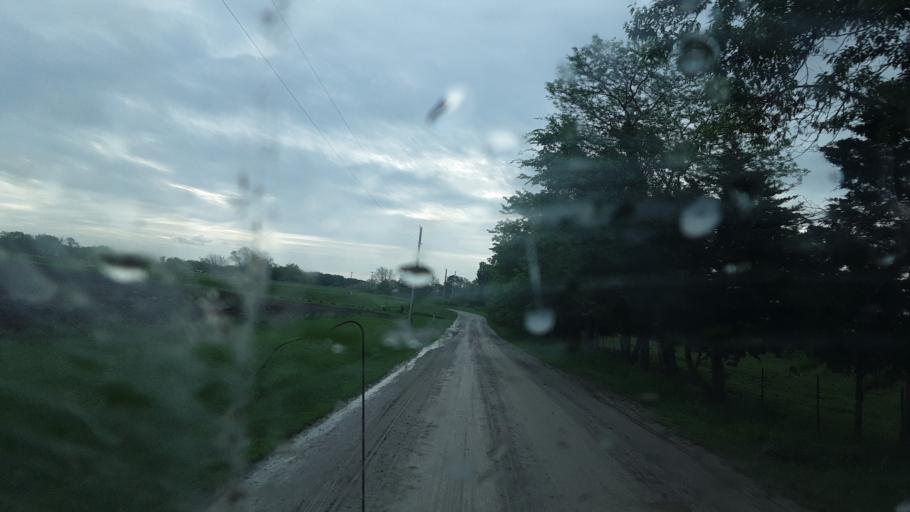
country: US
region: Missouri
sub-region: Clark County
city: Kahoka
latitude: 40.4423
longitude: -91.6125
